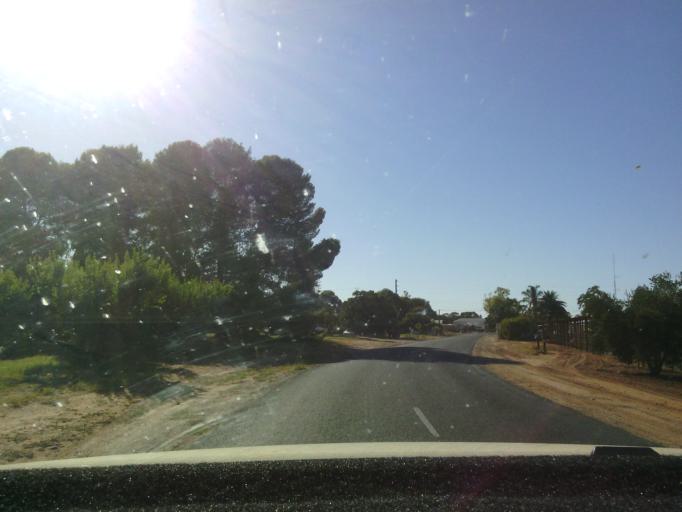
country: AU
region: South Australia
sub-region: Berri and Barmera
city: Berri
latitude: -34.2665
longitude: 140.6009
